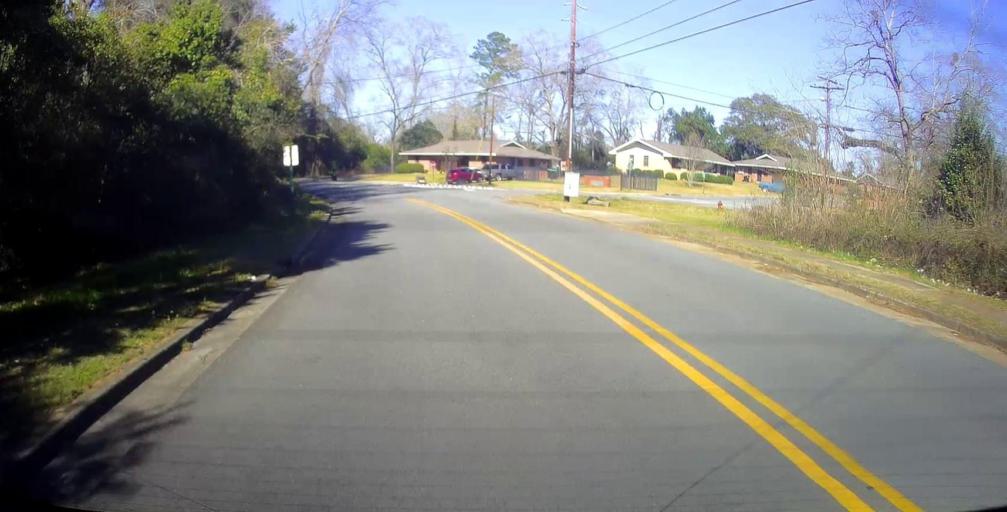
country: US
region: Georgia
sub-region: Macon County
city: Montezuma
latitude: 32.2890
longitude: -84.0298
